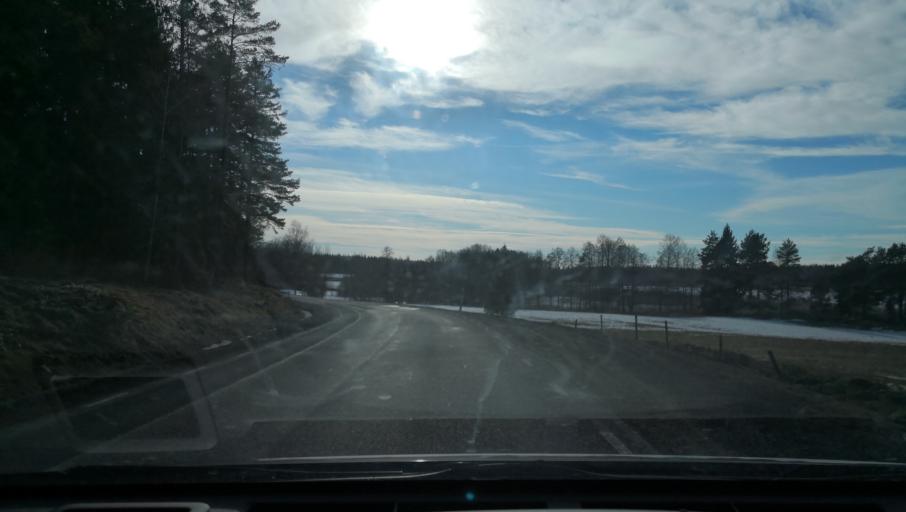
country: SE
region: Uppsala
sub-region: Osthammars Kommun
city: Osterbybruk
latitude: 60.2478
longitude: 17.9378
